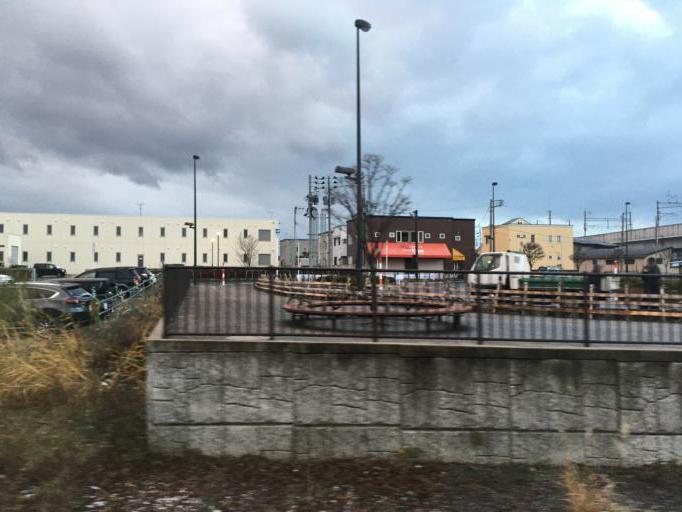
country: JP
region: Aomori
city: Aomori Shi
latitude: 40.8273
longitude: 140.6950
